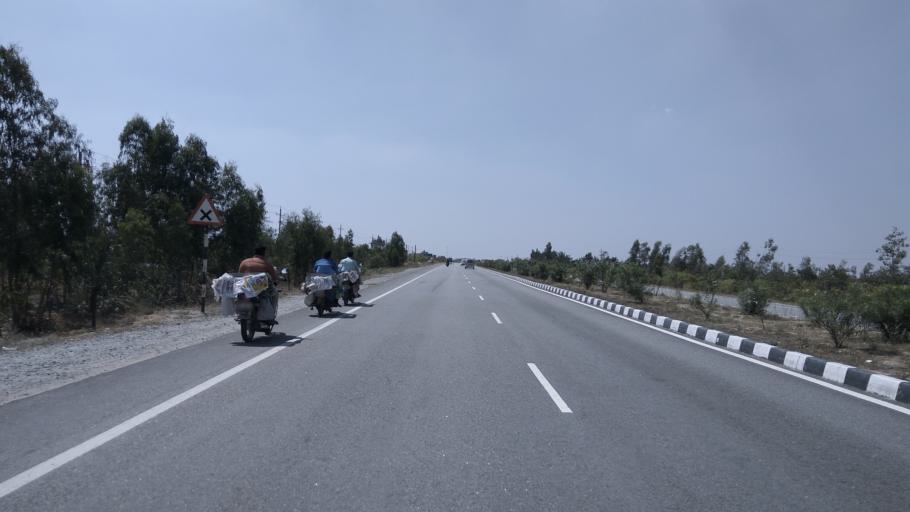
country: IN
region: Karnataka
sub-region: Kolar
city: Mulbagal
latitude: 13.1528
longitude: 78.3810
